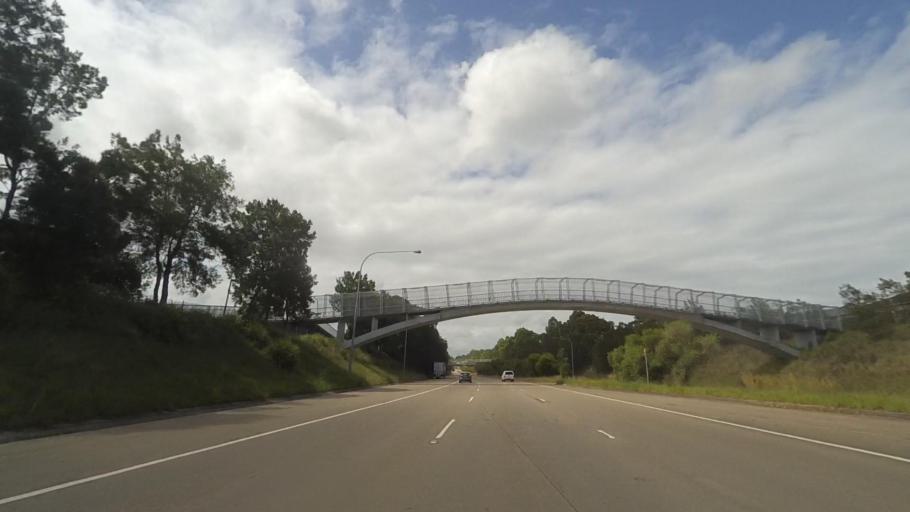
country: AU
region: New South Wales
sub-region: Newcastle
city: North Lambton
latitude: -32.9036
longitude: 151.6931
